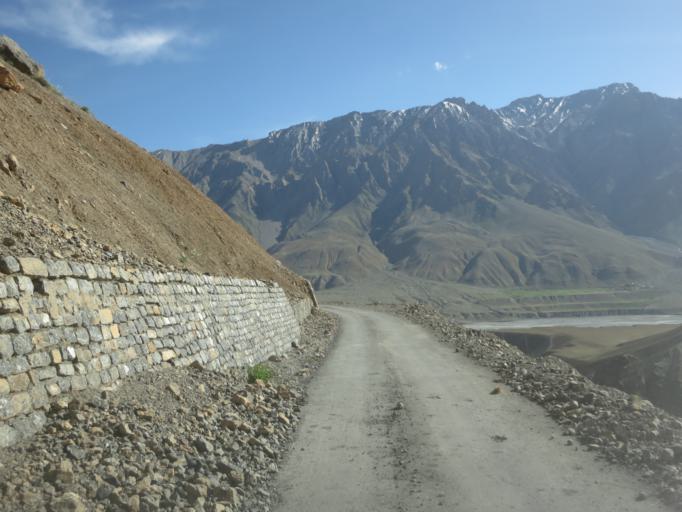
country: IN
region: Himachal Pradesh
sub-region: Shimla
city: Sarahan
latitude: 32.3116
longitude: 78.0035
